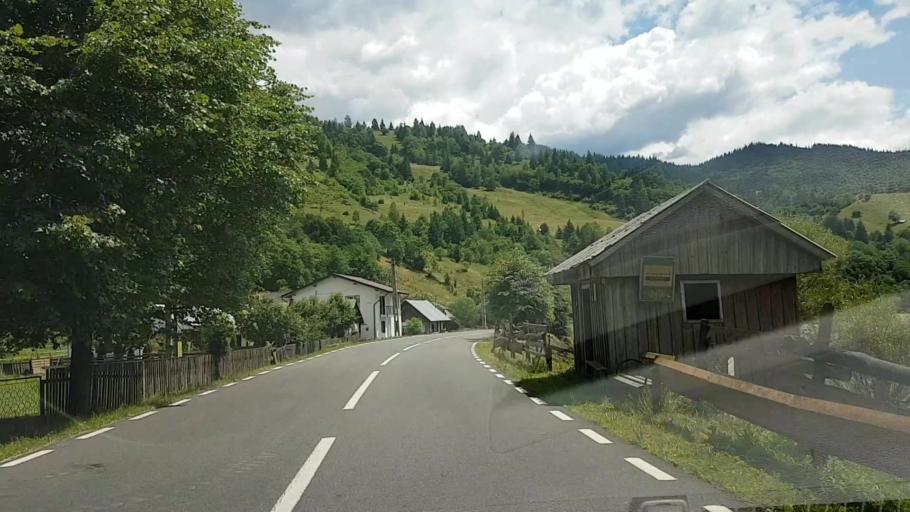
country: RO
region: Suceava
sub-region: Comuna Crucea
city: Crucea
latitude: 47.3912
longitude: 25.5769
